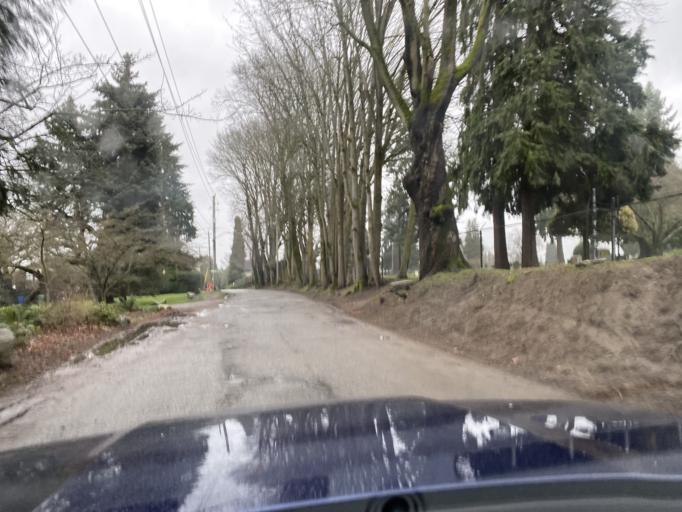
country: US
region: Washington
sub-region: King County
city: Seattle
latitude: 47.6361
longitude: -122.3163
